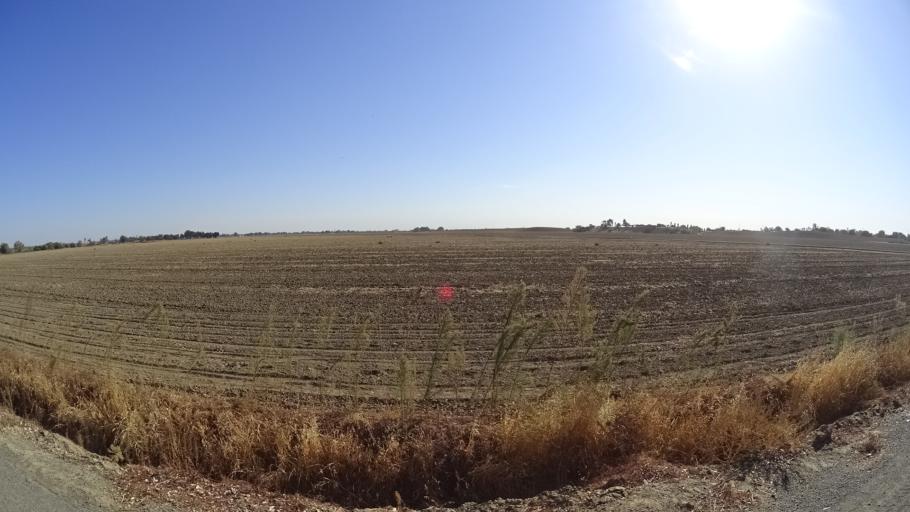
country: US
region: California
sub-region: Yolo County
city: Woodland
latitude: 38.6838
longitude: -121.8671
